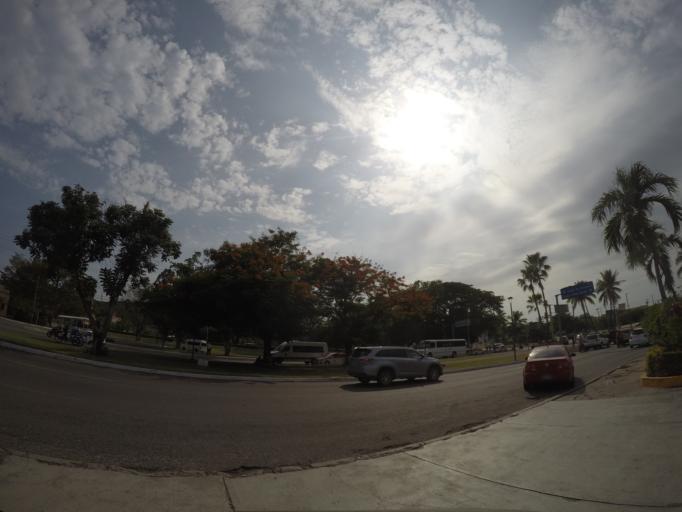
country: MX
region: Oaxaca
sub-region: Santa Maria Huatulco
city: Crucecita
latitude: 15.7655
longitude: -96.1349
